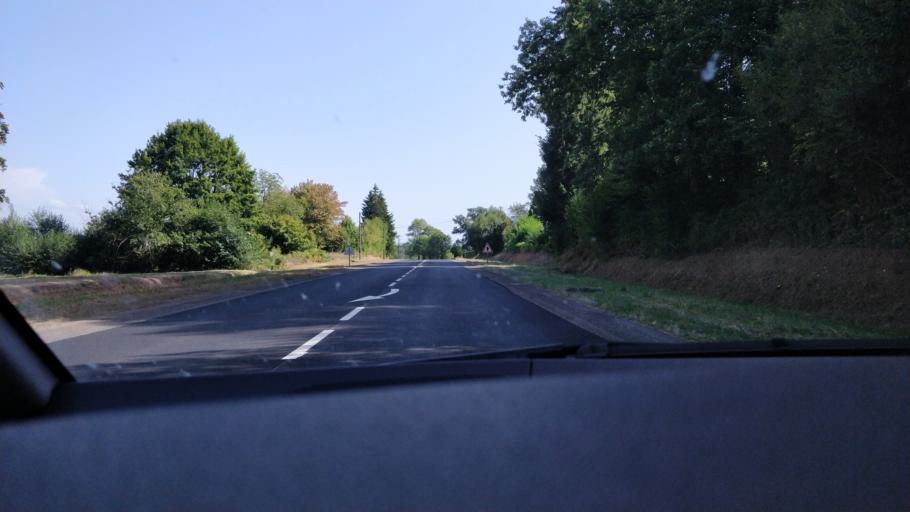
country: FR
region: Limousin
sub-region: Departement de la Correze
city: Uzerche
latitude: 45.4776
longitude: 1.5329
